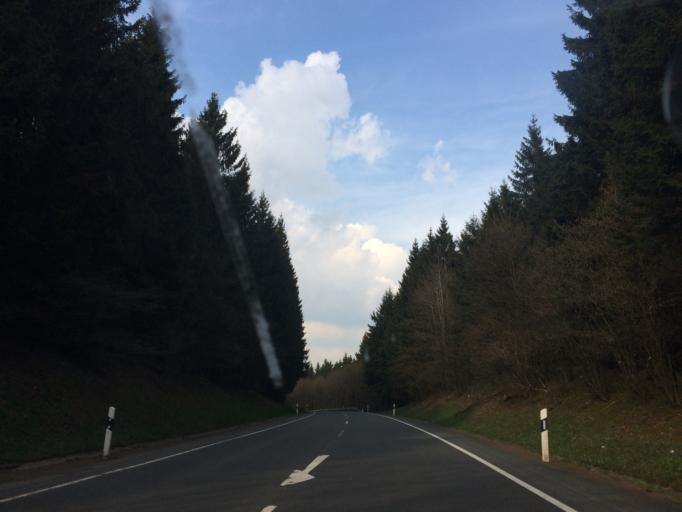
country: DE
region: North Rhine-Westphalia
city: Altena
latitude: 51.2720
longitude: 7.6337
